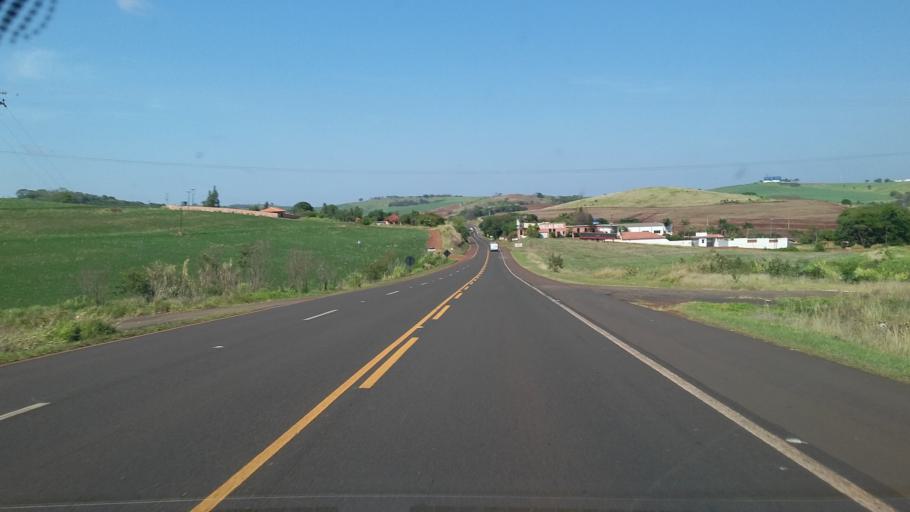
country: BR
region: Parana
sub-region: Bandeirantes
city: Bandeirantes
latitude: -23.1311
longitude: -50.3696
